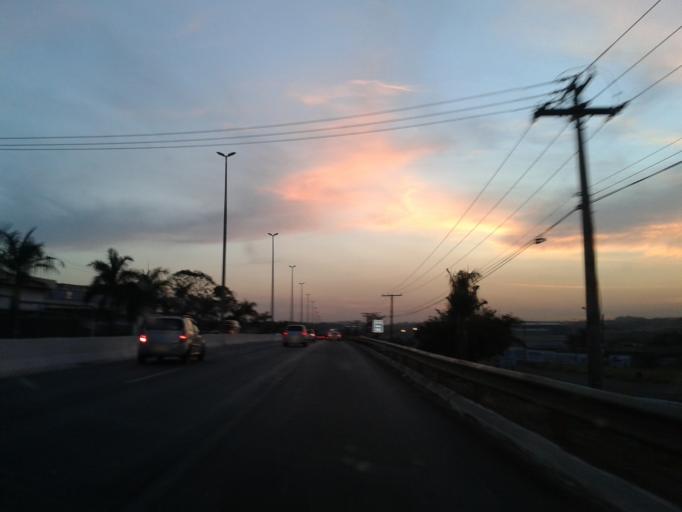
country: BR
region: Goias
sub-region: Goiania
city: Goiania
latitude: -16.6597
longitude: -49.3457
